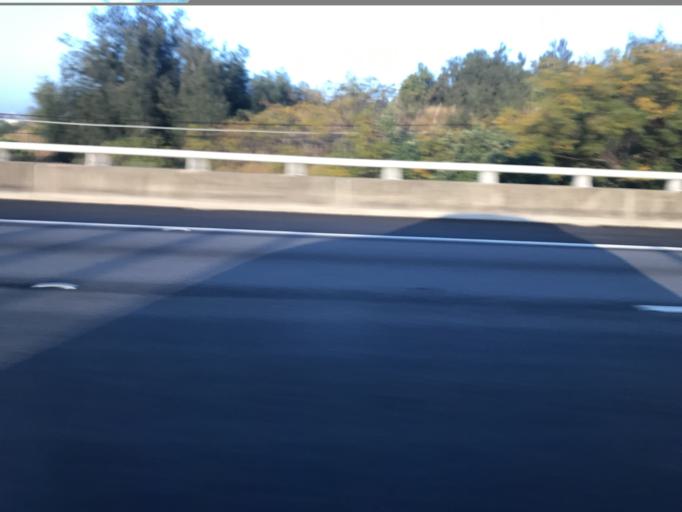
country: TW
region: Taiwan
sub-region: Miaoli
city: Miaoli
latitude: 24.6242
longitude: 120.8134
